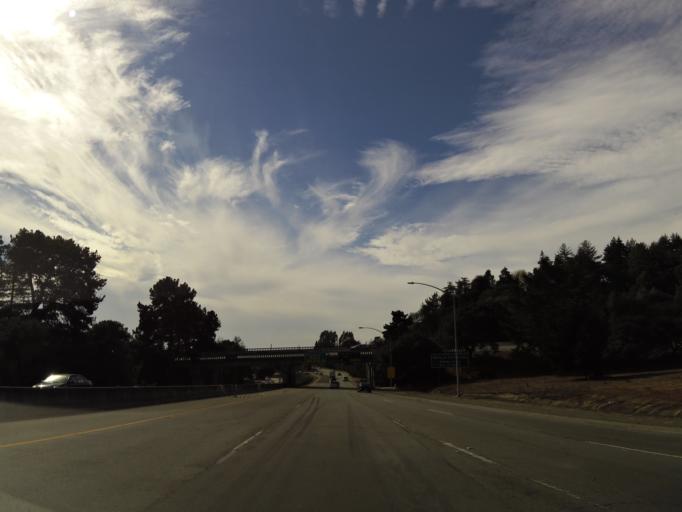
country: US
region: California
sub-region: Santa Cruz County
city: Pasatiempo
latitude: 36.9908
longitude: -122.0212
